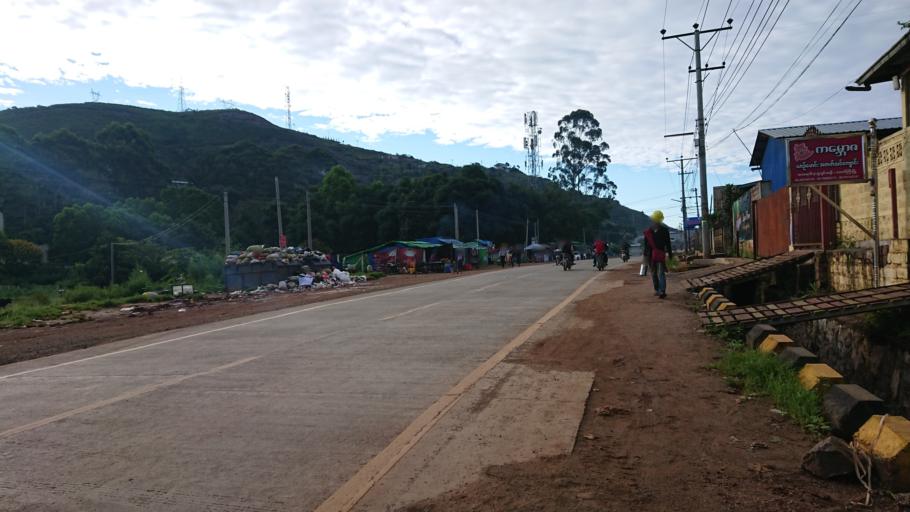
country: MM
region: Shan
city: Taunggyi
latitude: 20.7480
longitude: 97.0500
